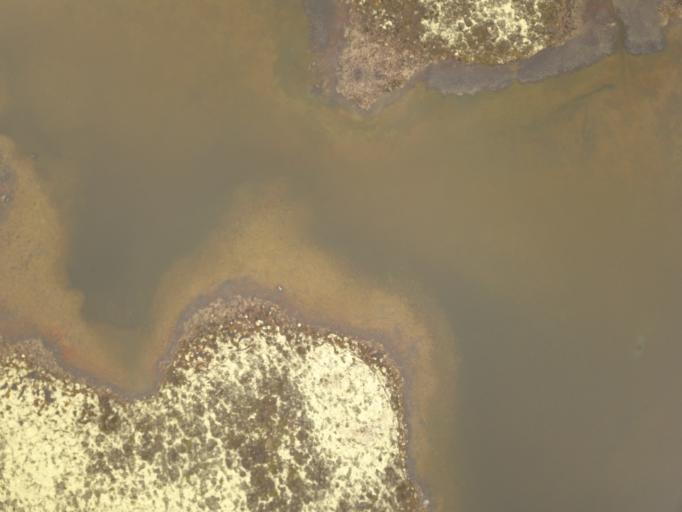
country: NO
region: Hedmark
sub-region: Folldal
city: Folldal
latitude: 62.2276
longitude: 9.6465
